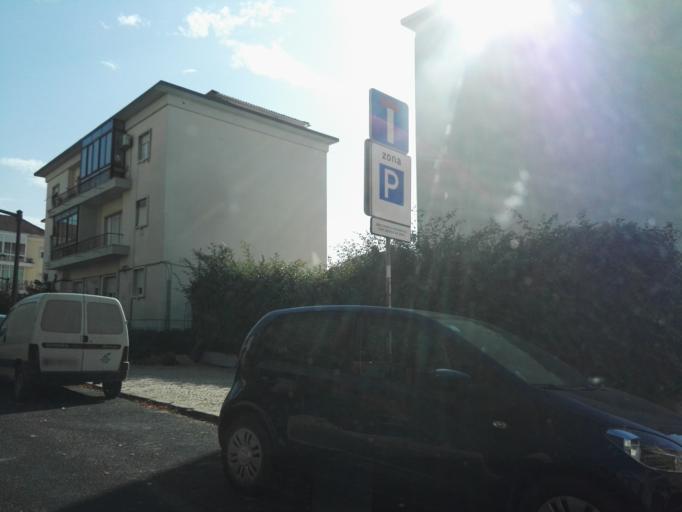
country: PT
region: Lisbon
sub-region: Lisbon
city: Lisbon
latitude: 38.7478
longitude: -9.1451
